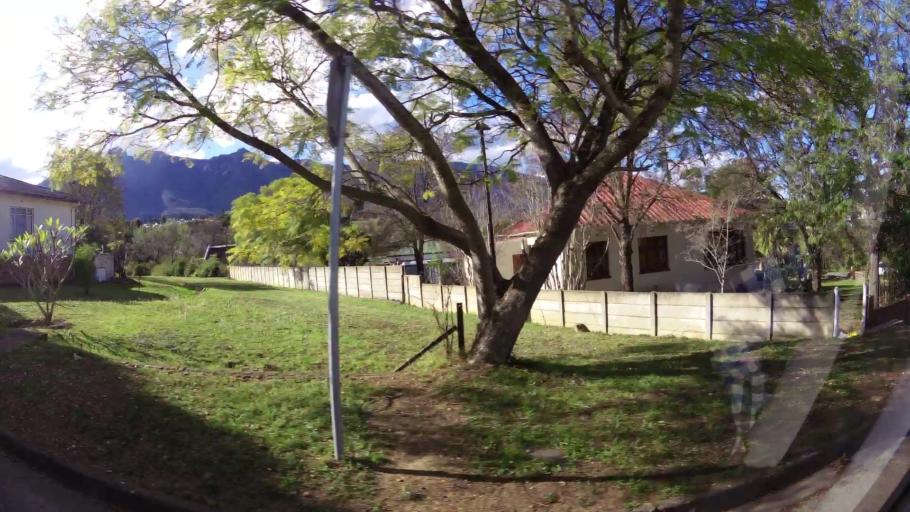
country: ZA
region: Western Cape
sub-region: Overberg District Municipality
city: Swellendam
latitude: -34.0206
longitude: 20.4397
